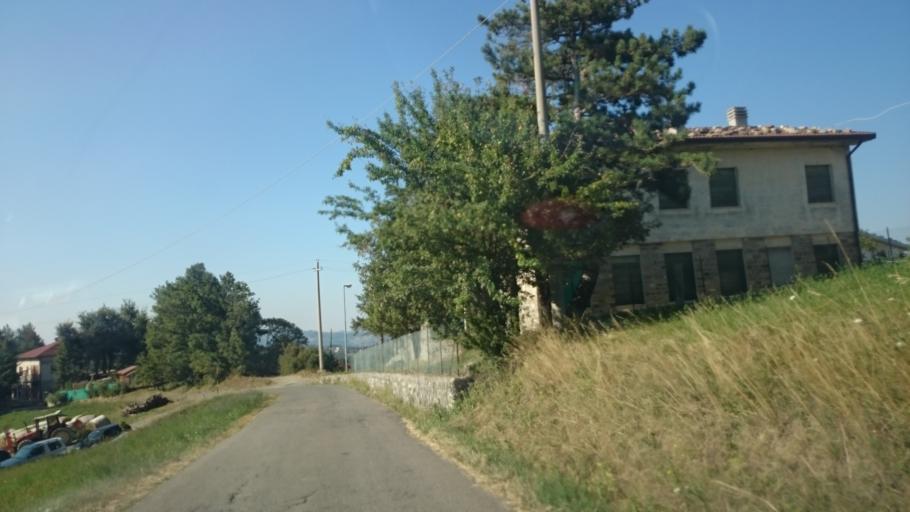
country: IT
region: Emilia-Romagna
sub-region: Provincia di Reggio Emilia
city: Villa Minozzo
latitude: 44.3351
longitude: 10.4734
